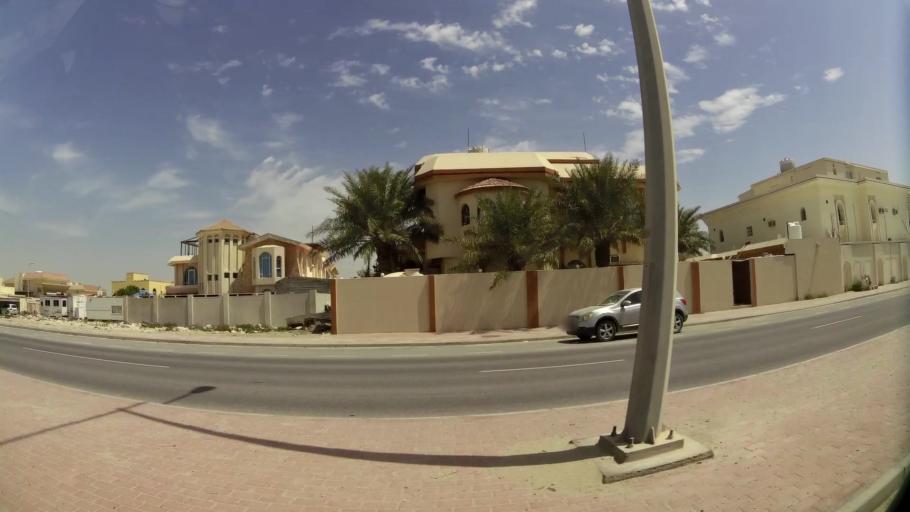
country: QA
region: Baladiyat ar Rayyan
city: Ar Rayyan
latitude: 25.2880
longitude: 51.4066
